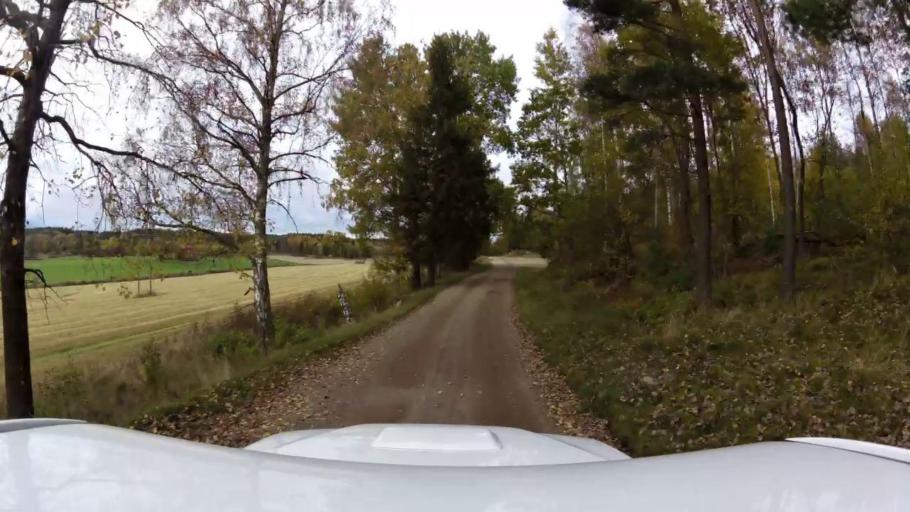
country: SE
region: OEstergoetland
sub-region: Linkopings Kommun
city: Ekangen
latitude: 58.5598
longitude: 15.6683
